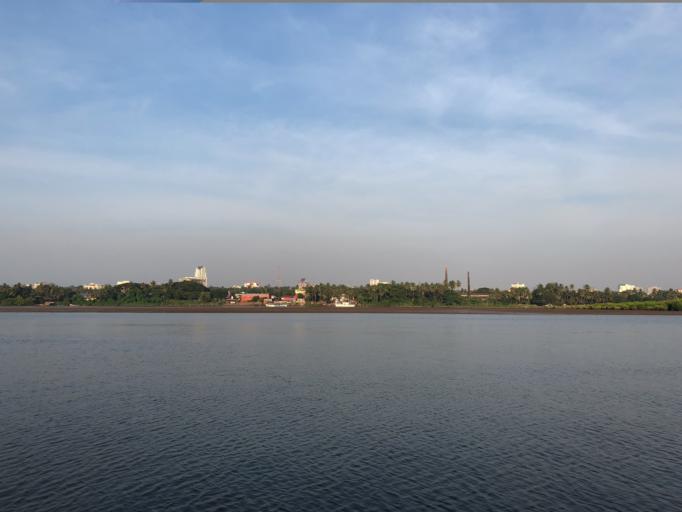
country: IN
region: Karnataka
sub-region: Dakshina Kannada
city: Mangalore
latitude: 12.8788
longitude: 74.8209
